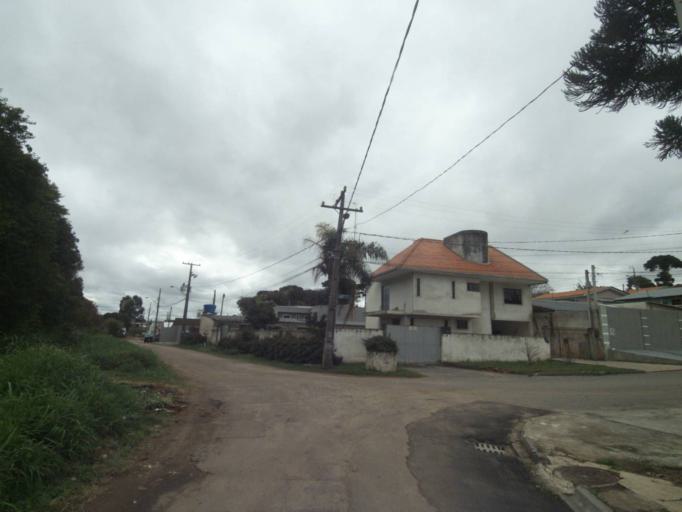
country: BR
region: Parana
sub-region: Sao Jose Dos Pinhais
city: Sao Jose dos Pinhais
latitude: -25.5410
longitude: -49.2998
